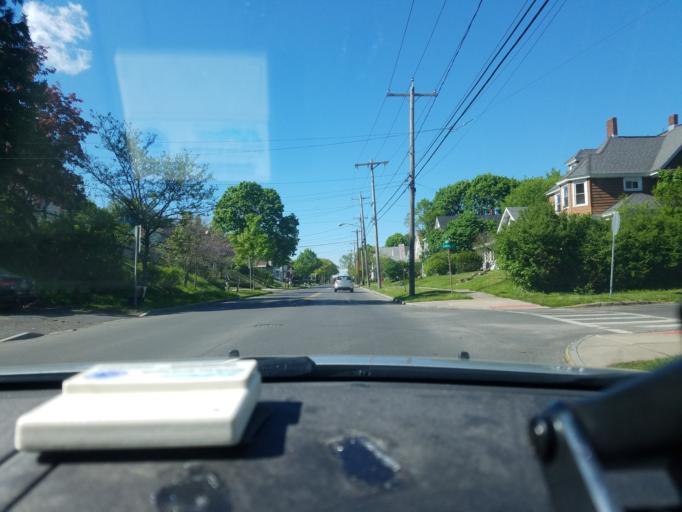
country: US
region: New York
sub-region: Onondaga County
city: Lyncourt
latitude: 43.0595
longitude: -76.1223
